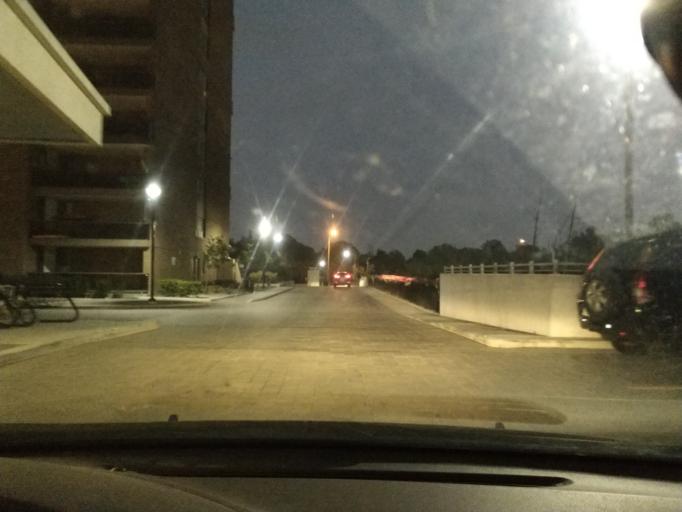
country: CA
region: Ontario
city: Brampton
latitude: 43.7084
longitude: -79.7260
